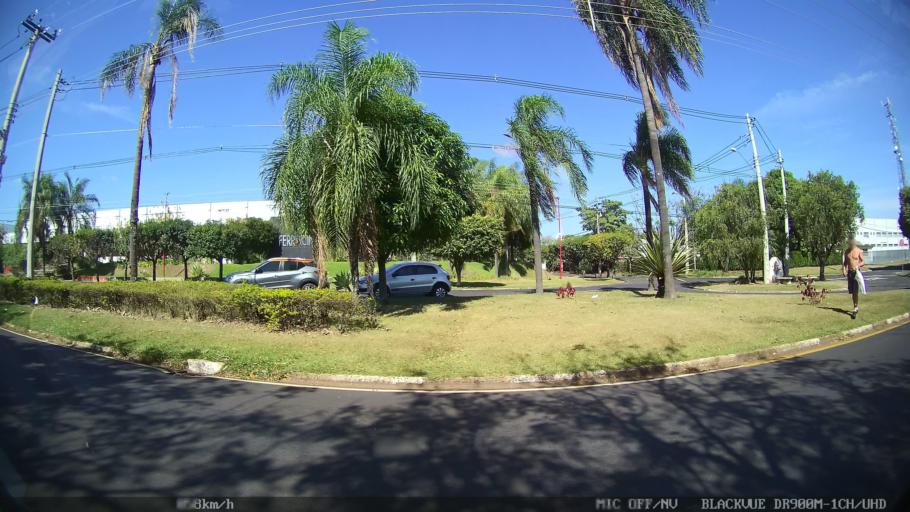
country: BR
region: Sao Paulo
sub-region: Franca
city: Franca
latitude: -20.5473
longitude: -47.4343
